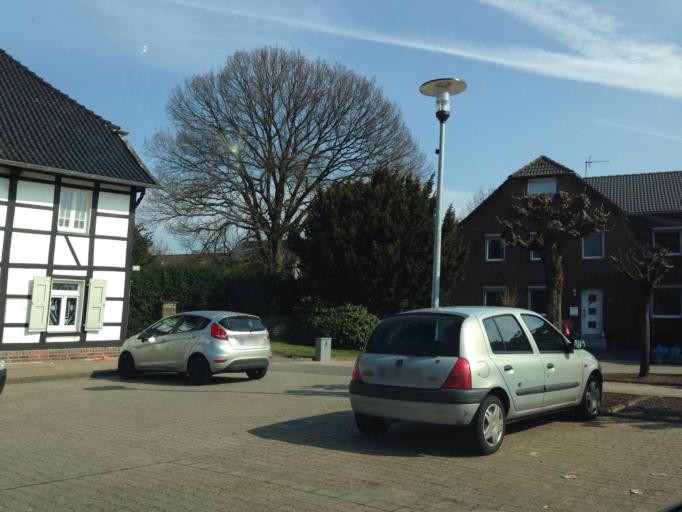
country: DE
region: North Rhine-Westphalia
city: Wegberg
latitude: 51.1022
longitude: 6.2746
